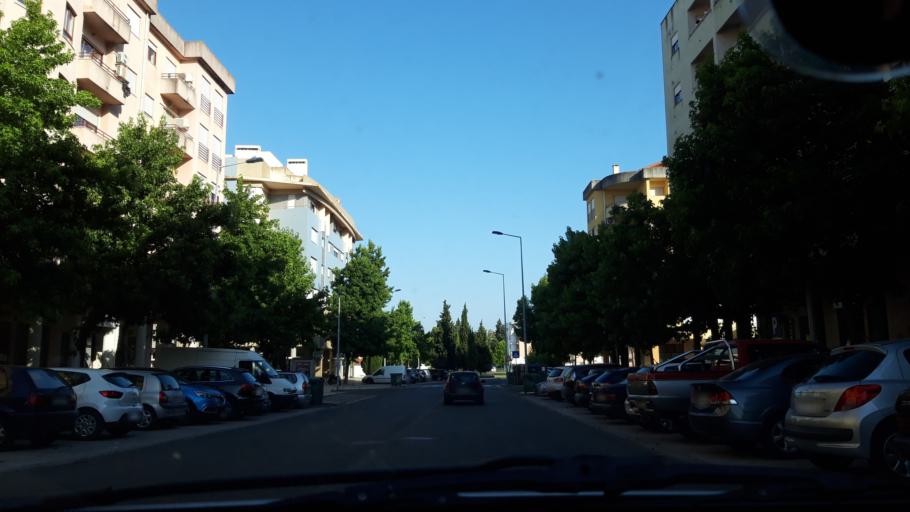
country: PT
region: Santarem
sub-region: Torres Novas
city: Torres Novas
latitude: 39.4759
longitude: -8.5493
